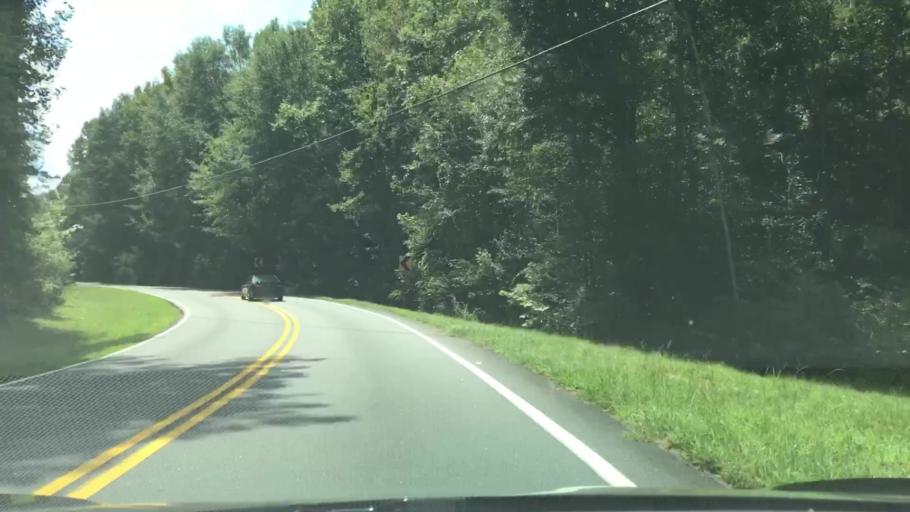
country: US
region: Georgia
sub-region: Gwinnett County
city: Snellville
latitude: 33.9011
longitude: -84.0683
